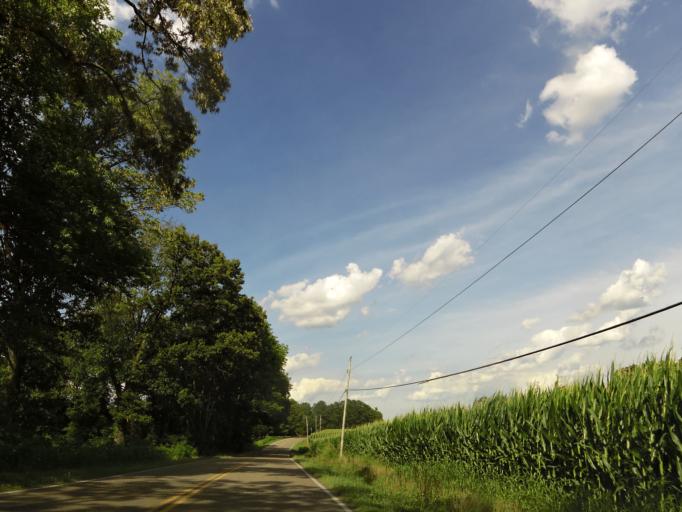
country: US
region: Tennessee
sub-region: Carroll County
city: Huntingdon
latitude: 36.0304
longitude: -88.3585
